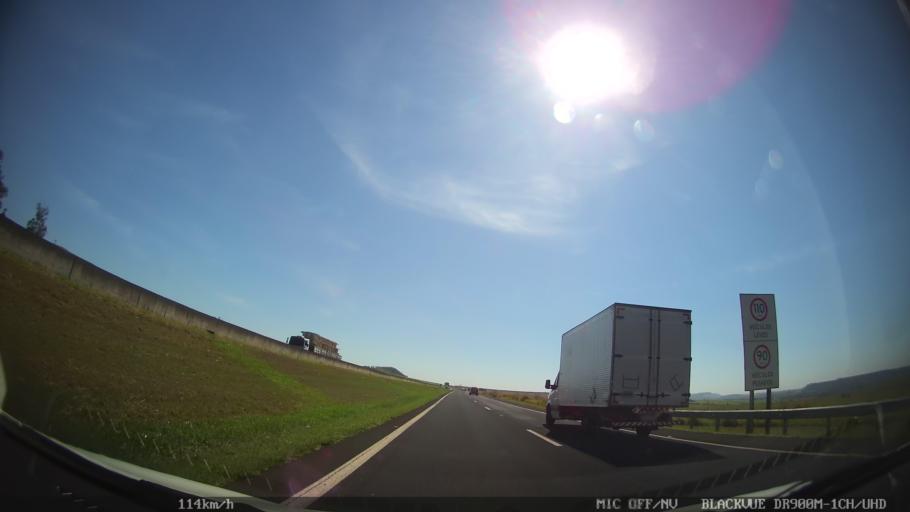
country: BR
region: Sao Paulo
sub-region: Sao Simao
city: Sao Simao
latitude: -21.4505
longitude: -47.6468
